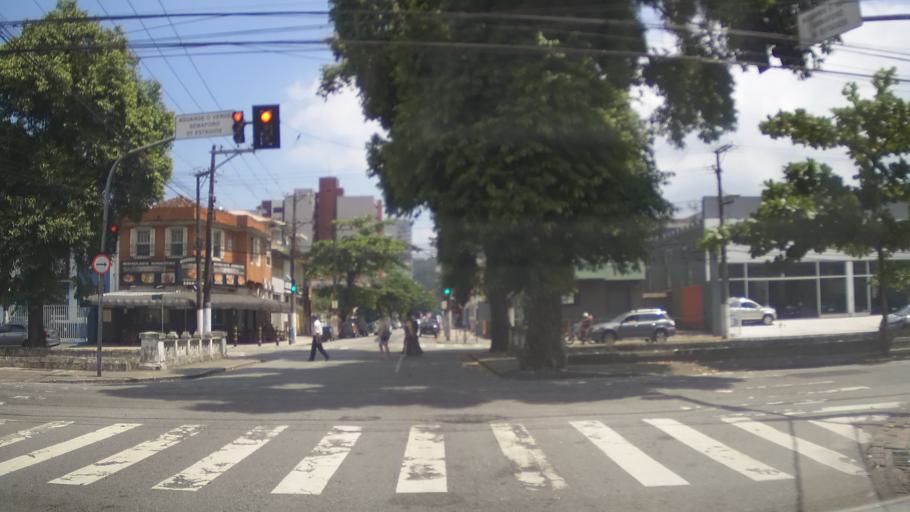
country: BR
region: Sao Paulo
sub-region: Santos
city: Santos
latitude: -23.9499
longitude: -46.3255
